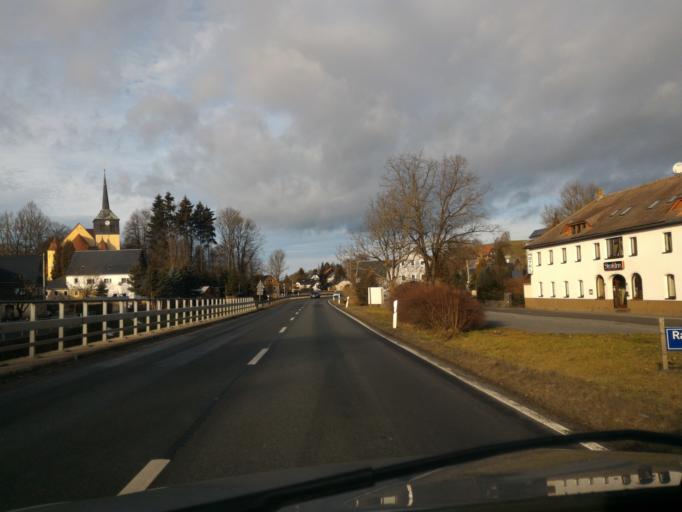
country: DE
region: Saxony
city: Neusalza-Spremberg
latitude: 51.0383
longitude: 14.5381
